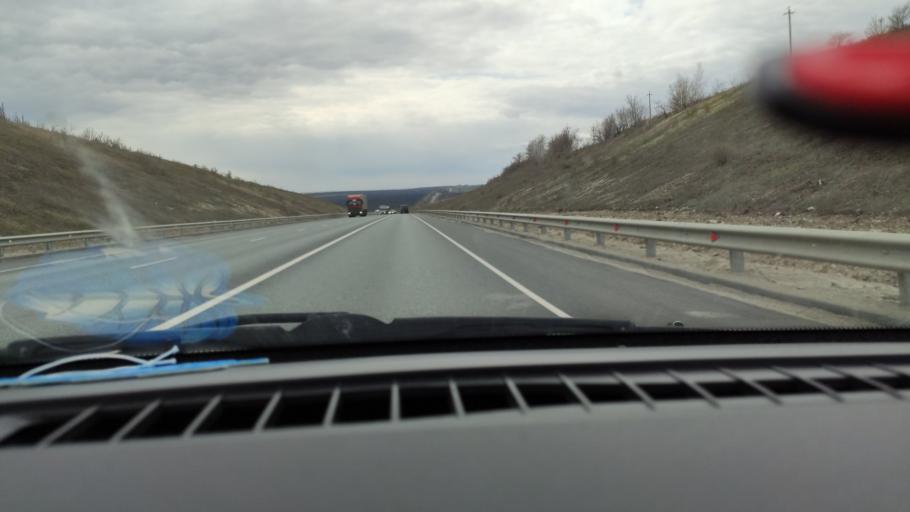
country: RU
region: Saratov
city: Yelshanka
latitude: 51.8826
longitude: 46.5123
